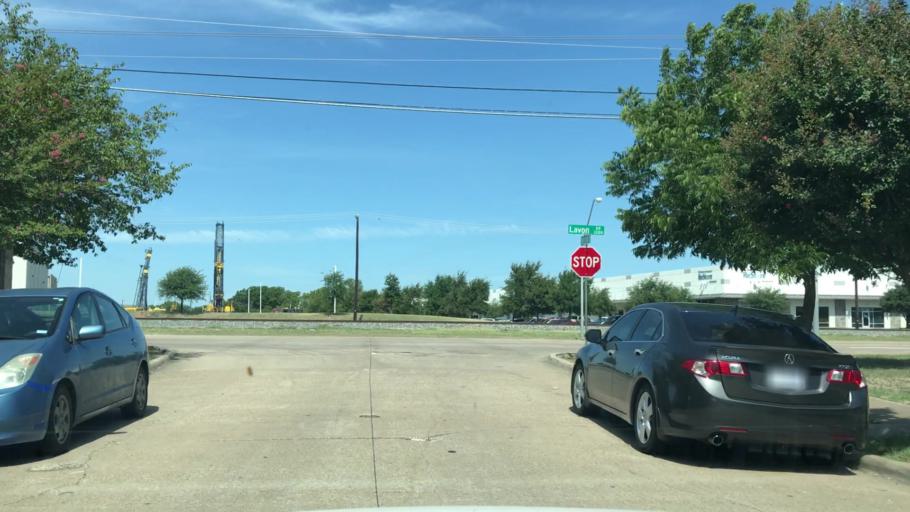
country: US
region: Texas
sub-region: Dallas County
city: Garland
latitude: 32.9344
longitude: -96.6242
